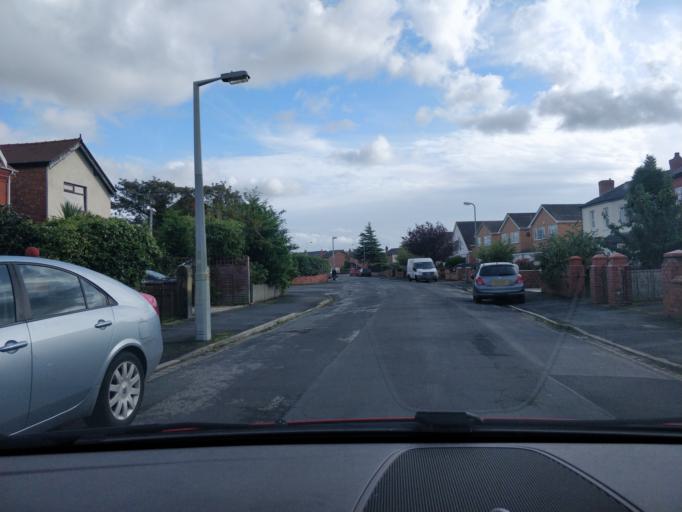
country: GB
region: England
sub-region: Sefton
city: Southport
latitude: 53.6218
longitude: -3.0172
